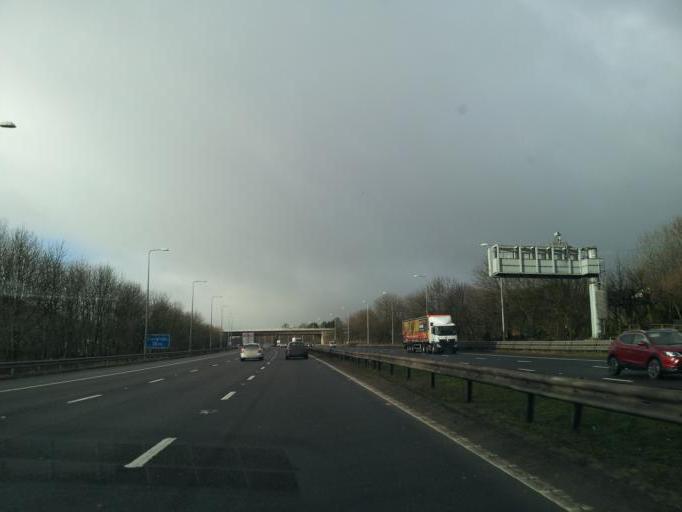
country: GB
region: England
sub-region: Kirklees
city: Linthwaite
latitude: 53.6531
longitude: -1.8790
